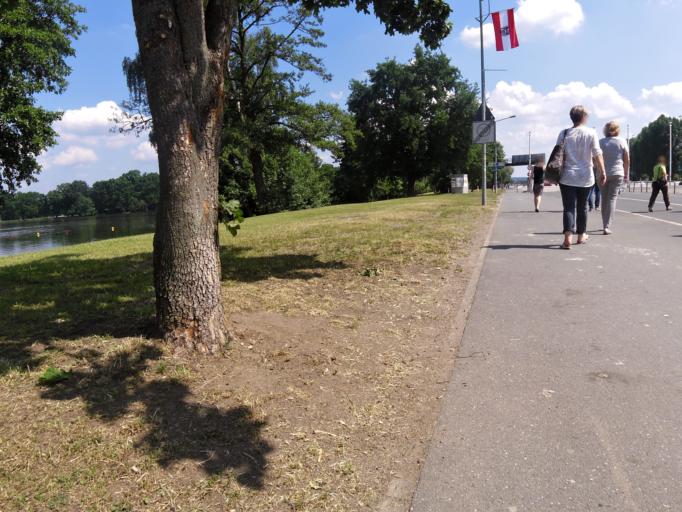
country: DE
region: Bavaria
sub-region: Regierungsbezirk Mittelfranken
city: Nuernberg
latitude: 49.4291
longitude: 11.1118
